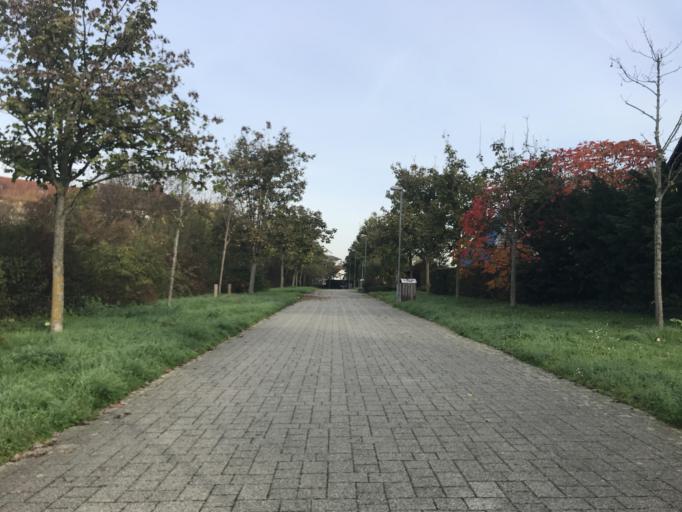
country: DE
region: Rheinland-Pfalz
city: Mainz
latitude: 50.0160
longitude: 8.2988
